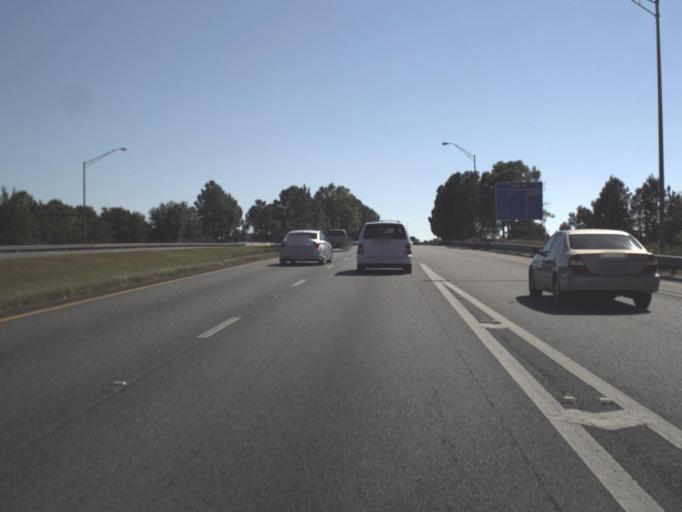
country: US
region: Florida
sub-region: Seminole County
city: Oviedo
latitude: 28.6838
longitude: -81.2265
